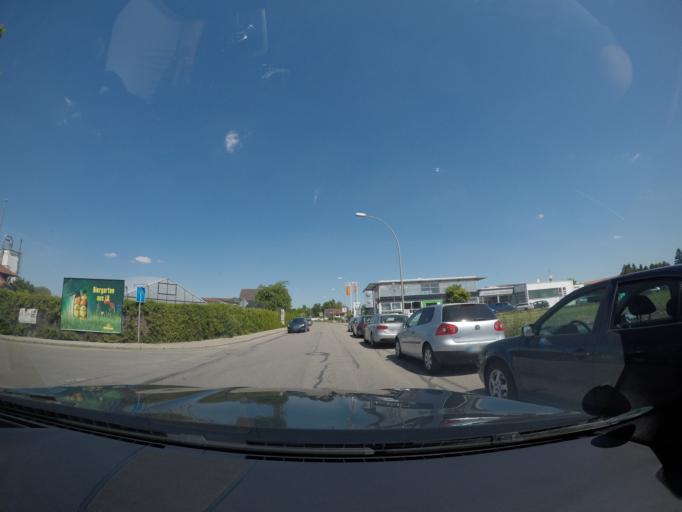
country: DE
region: Bavaria
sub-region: Lower Bavaria
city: Tiefenbach
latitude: 48.5372
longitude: 12.1196
